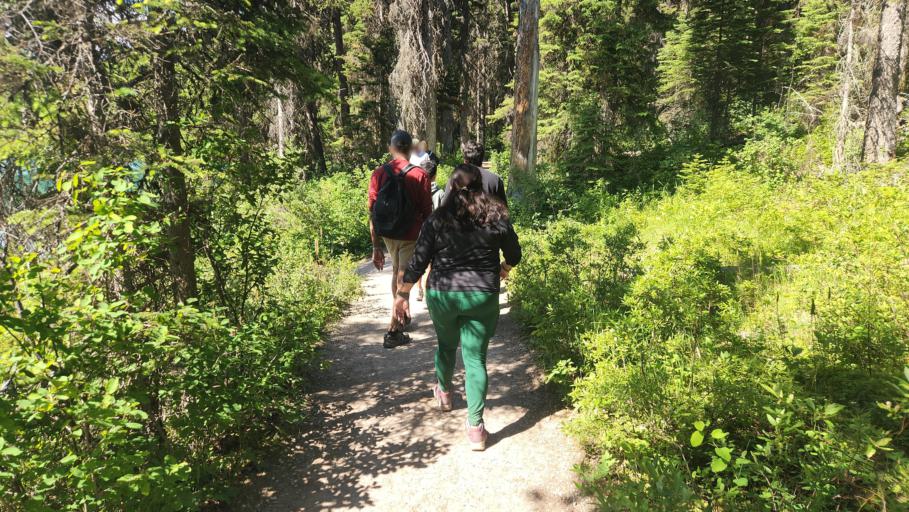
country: CA
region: Alberta
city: Lake Louise
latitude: 51.4433
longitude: -116.5396
